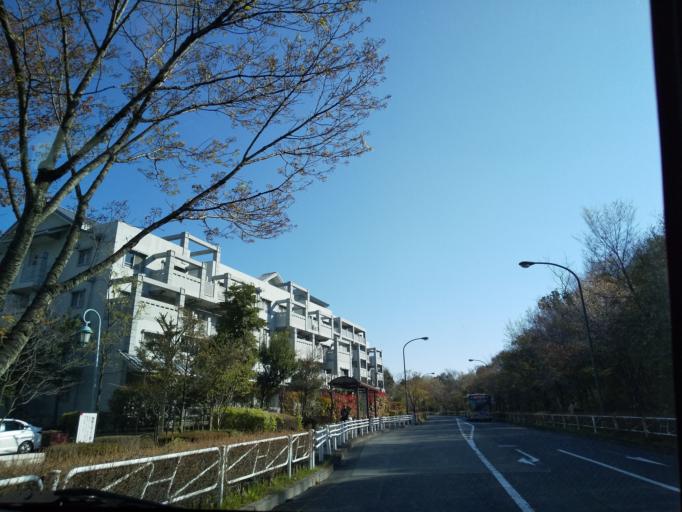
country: JP
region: Tokyo
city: Hino
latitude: 35.6084
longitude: 139.3888
